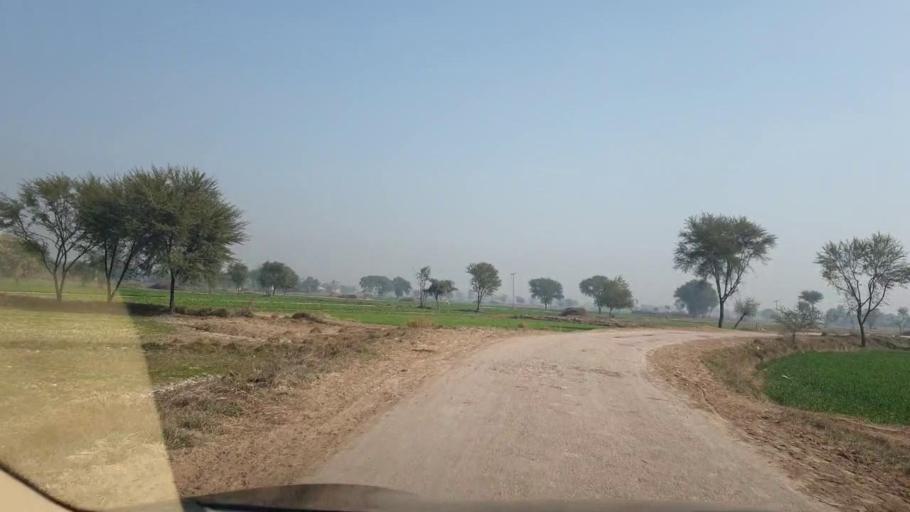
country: PK
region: Sindh
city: Ubauro
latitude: 28.1142
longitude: 69.7318
